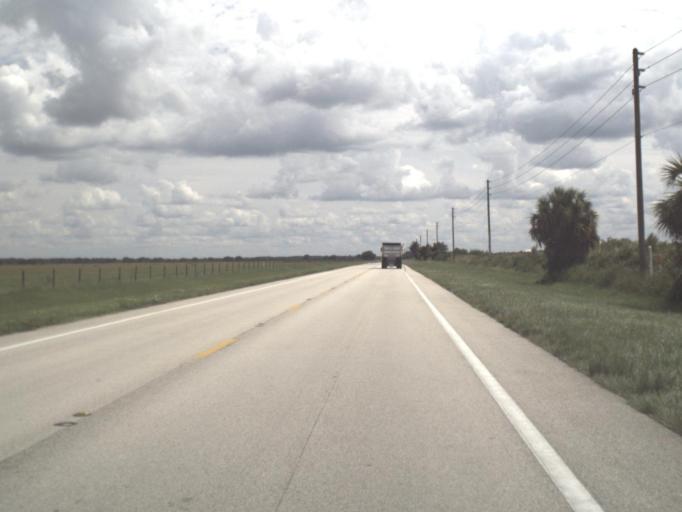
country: US
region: Florida
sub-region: DeSoto County
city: Nocatee
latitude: 27.0483
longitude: -81.7820
